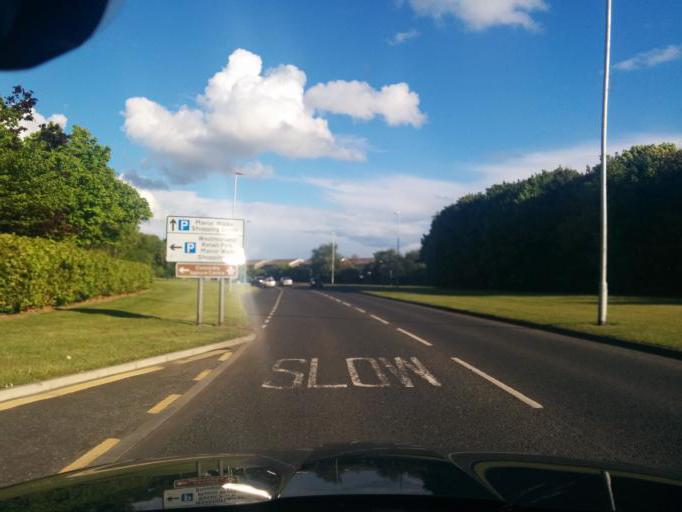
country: GB
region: England
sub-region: Northumberland
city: Cramlington
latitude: 55.0850
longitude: -1.5957
